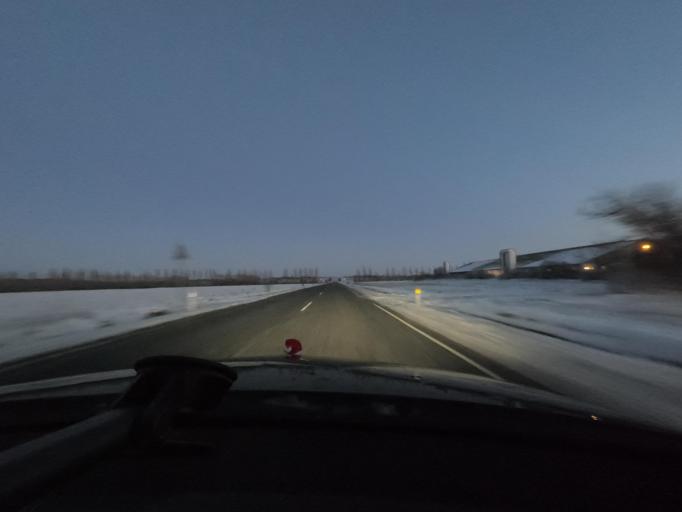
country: DK
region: South Denmark
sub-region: Tonder Kommune
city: Sherrebek
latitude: 55.1773
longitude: 8.8124
